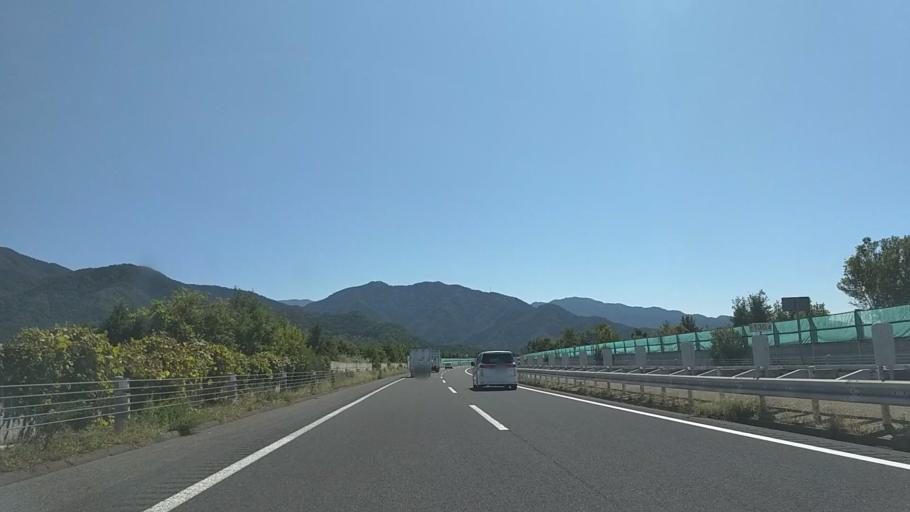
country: JP
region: Nagano
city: Suzaka
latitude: 36.6482
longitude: 138.2800
